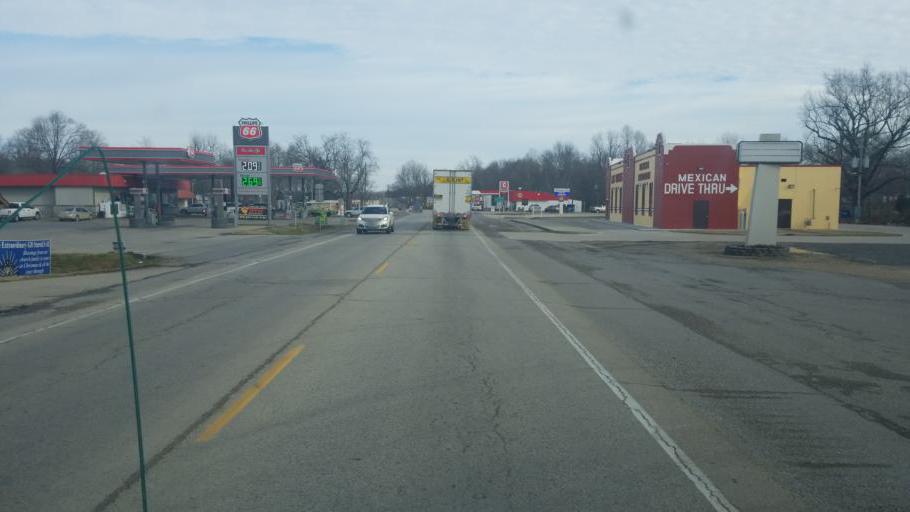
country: US
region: Missouri
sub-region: Stoddard County
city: Bloomfield
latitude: 36.8821
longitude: -89.9252
